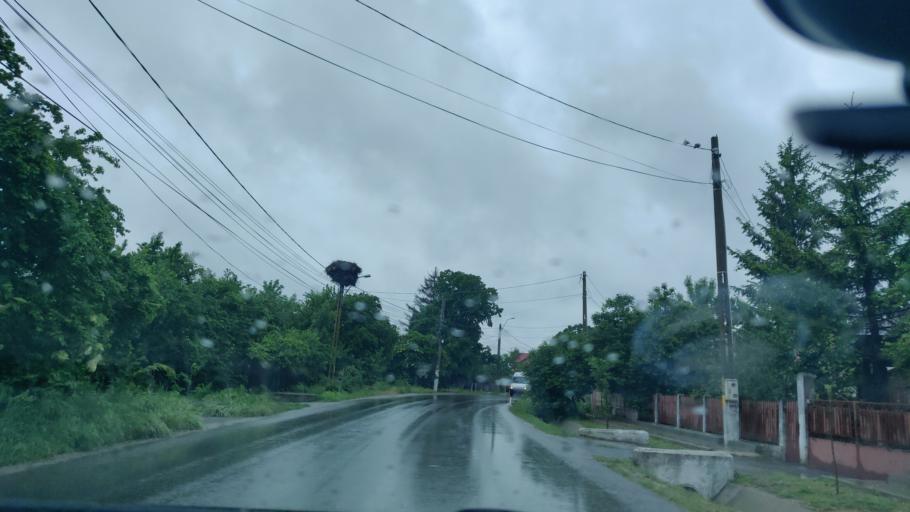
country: RO
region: Giurgiu
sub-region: Comuna Bulbucata
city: Bulbucata
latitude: 44.2741
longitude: 25.8267
